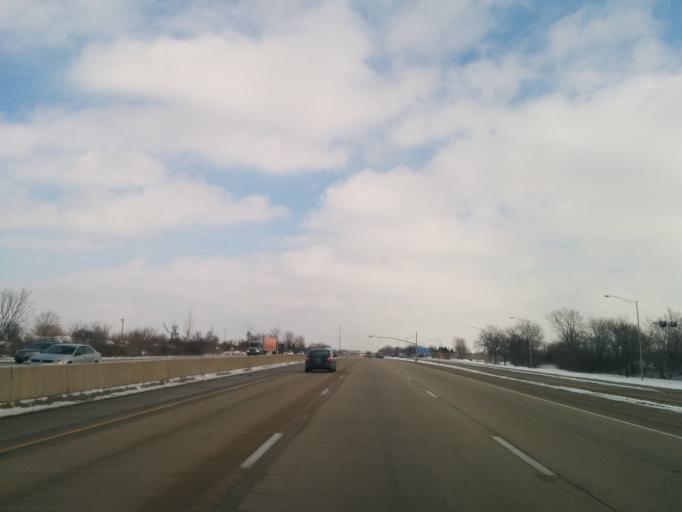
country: US
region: Illinois
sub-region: Will County
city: Mokena
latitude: 41.5522
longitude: -87.9055
